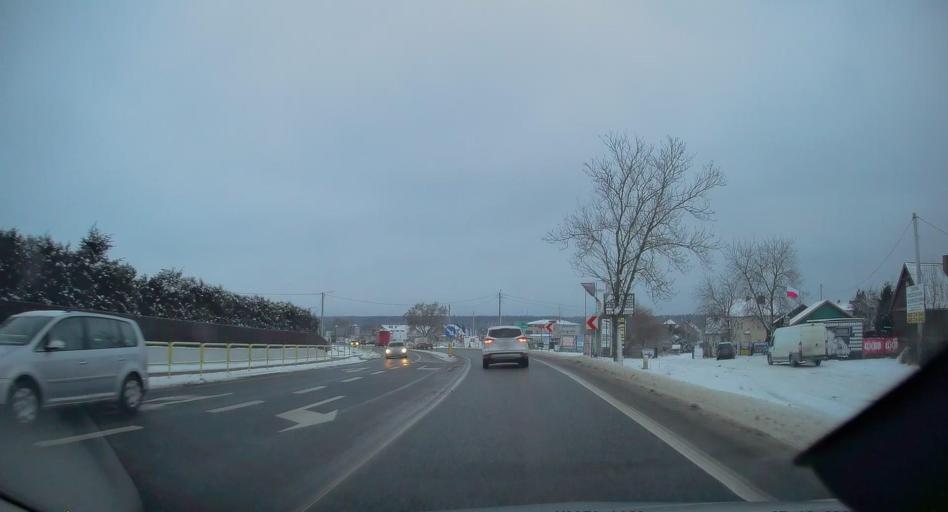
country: PL
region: Swietokrzyskie
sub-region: Powiat kielecki
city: Kostomloty Drugie
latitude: 50.9263
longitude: 20.5654
